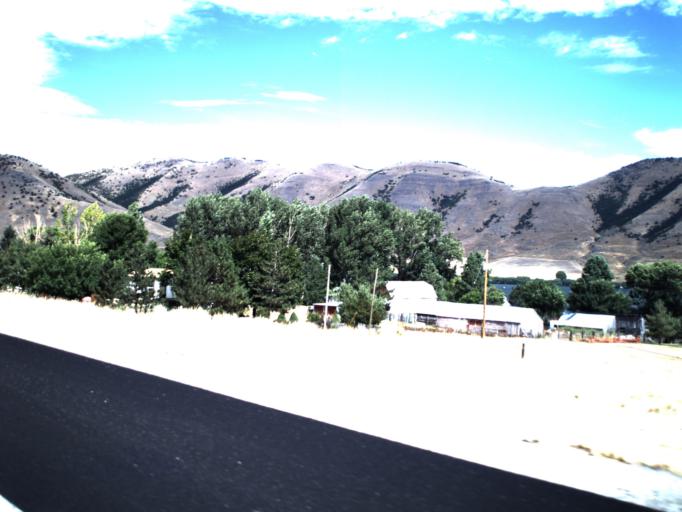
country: US
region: Utah
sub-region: Box Elder County
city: Brigham City
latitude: 41.5029
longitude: -111.9459
